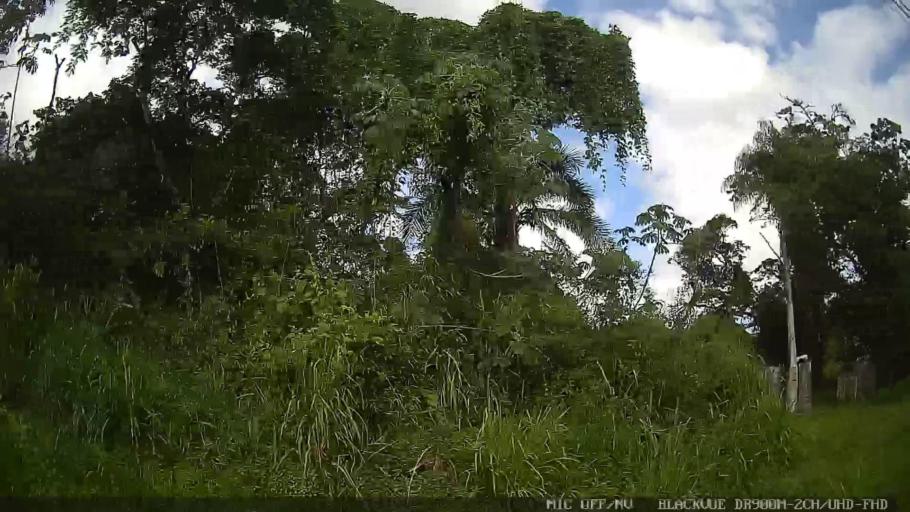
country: BR
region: Sao Paulo
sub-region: Peruibe
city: Peruibe
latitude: -24.2969
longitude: -47.0307
